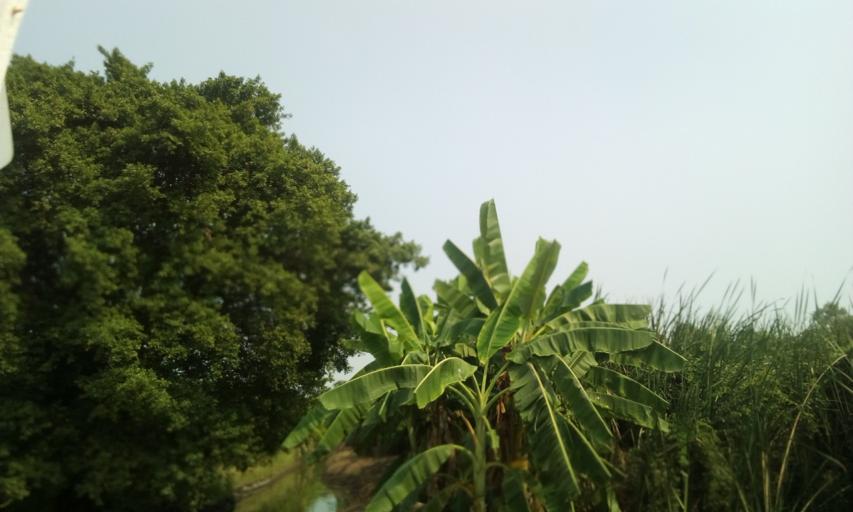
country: TH
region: Pathum Thani
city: Lam Luk Ka
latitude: 13.9403
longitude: 100.7241
